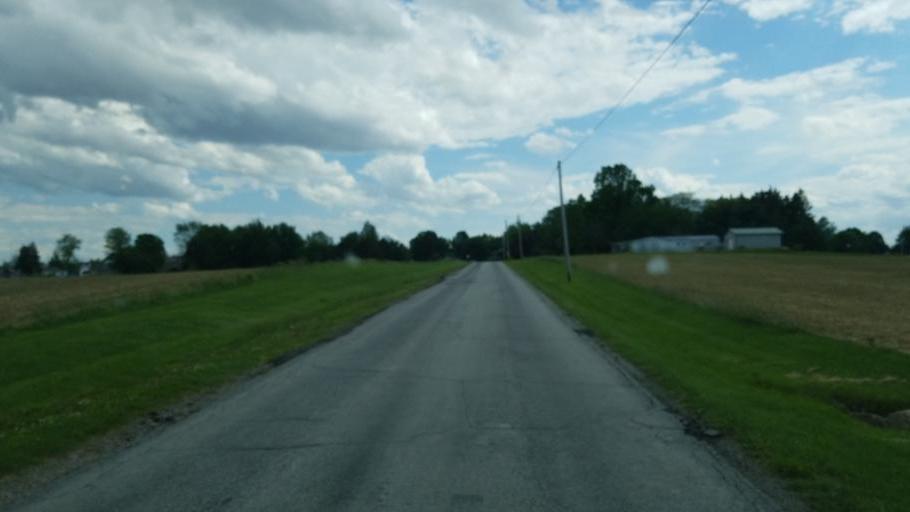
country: US
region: Ohio
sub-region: Huron County
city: Plymouth
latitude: 40.9723
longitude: -82.6070
